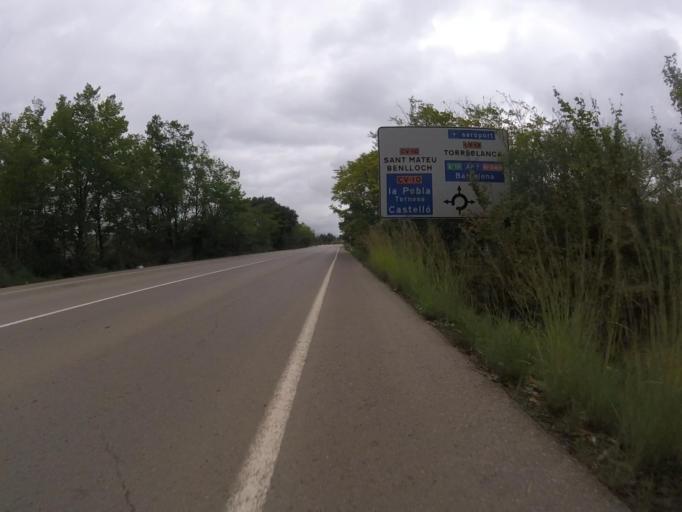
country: ES
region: Valencia
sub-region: Provincia de Castello
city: Cabanes
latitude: 40.1652
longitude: 0.0418
